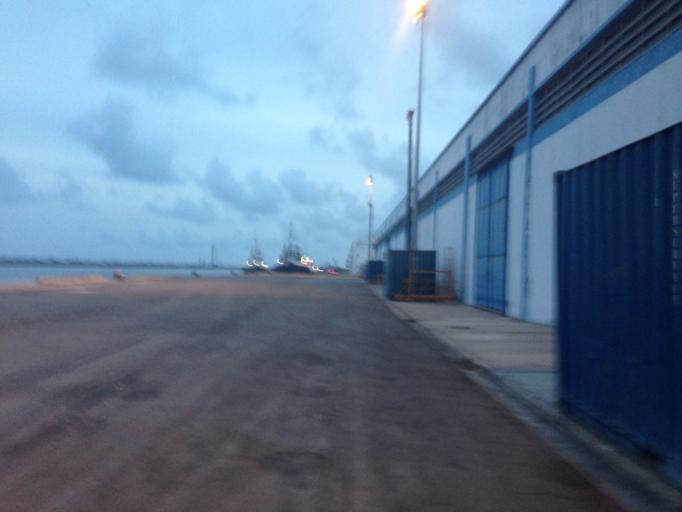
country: BR
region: Pernambuco
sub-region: Recife
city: Recife
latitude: -8.0552
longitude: -34.8681
